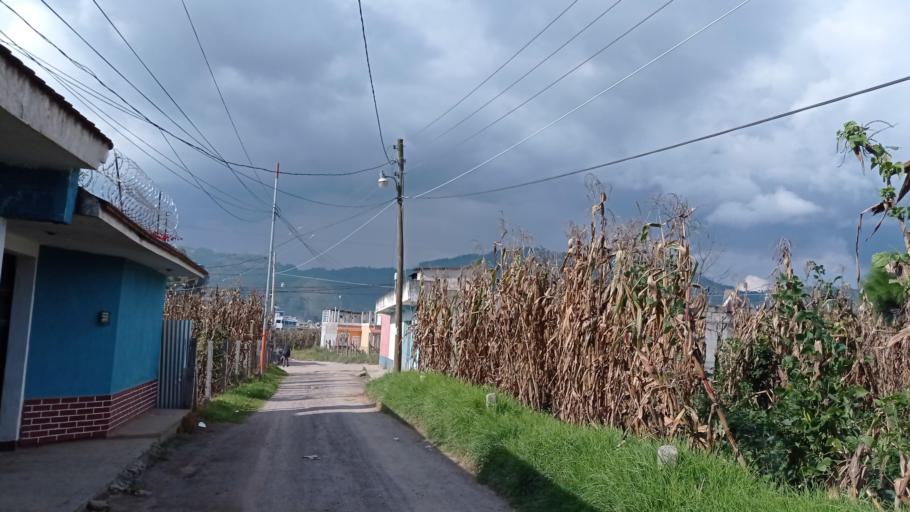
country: GT
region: Quetzaltenango
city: Olintepeque
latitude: 14.8692
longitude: -91.5014
